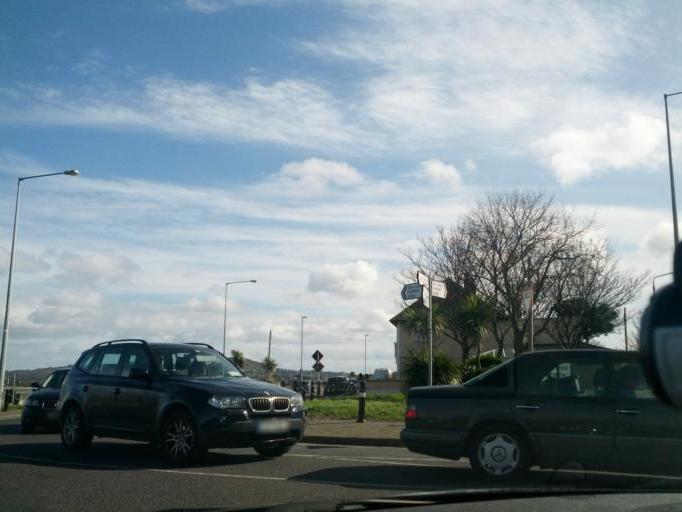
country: IE
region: Leinster
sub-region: Fingal County
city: Baldoyle
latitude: 53.3985
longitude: -6.1271
